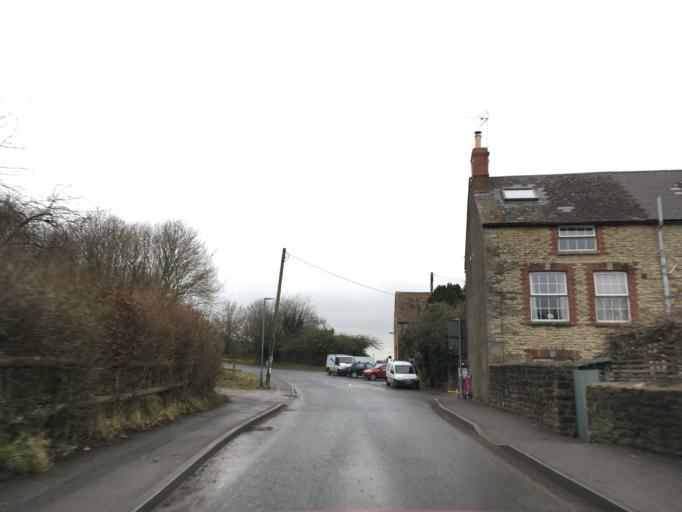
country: GB
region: England
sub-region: Gloucestershire
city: Wotton-under-Edge
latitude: 51.6268
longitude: -2.3689
